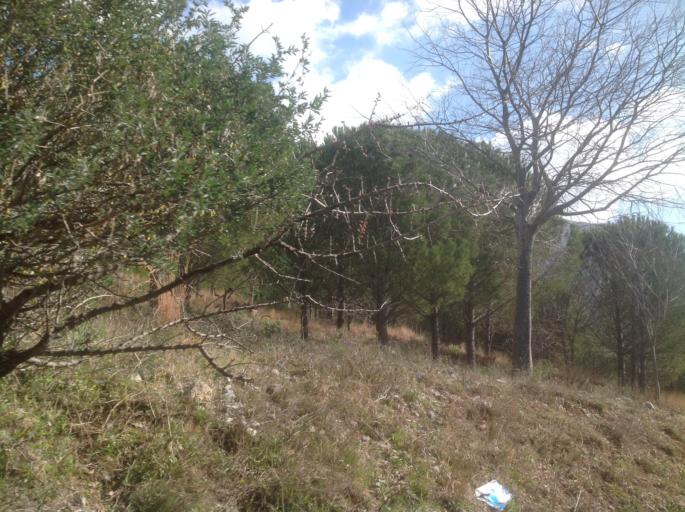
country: IT
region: Calabria
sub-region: Provincia di Cosenza
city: Frascineto
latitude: 39.8378
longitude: 16.2652
